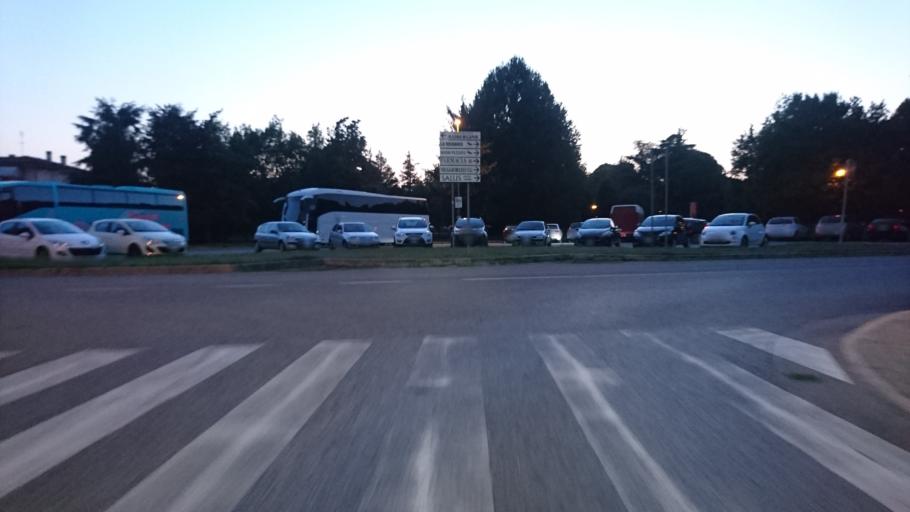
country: IT
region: Veneto
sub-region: Provincia di Padova
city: Abano Terme
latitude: 45.3510
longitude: 11.7755
